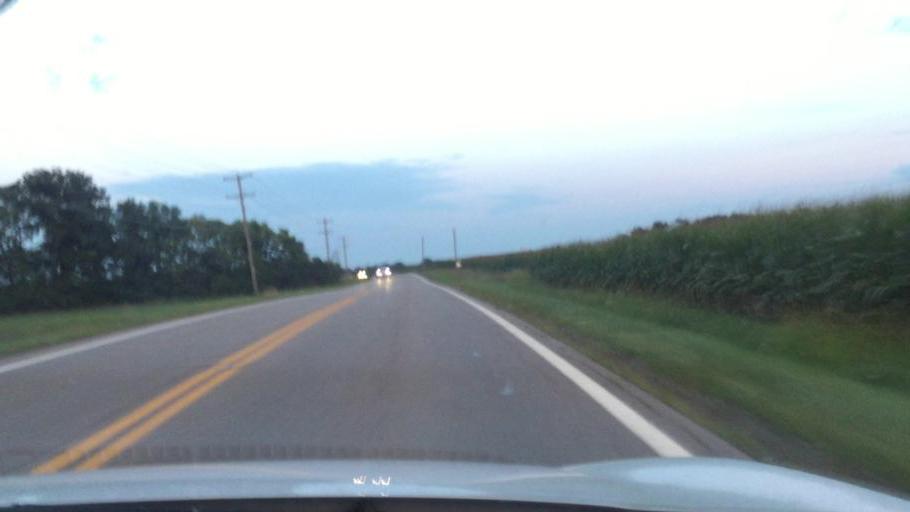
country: US
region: Ohio
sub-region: Madison County
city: West Jefferson
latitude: 39.9717
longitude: -83.3721
